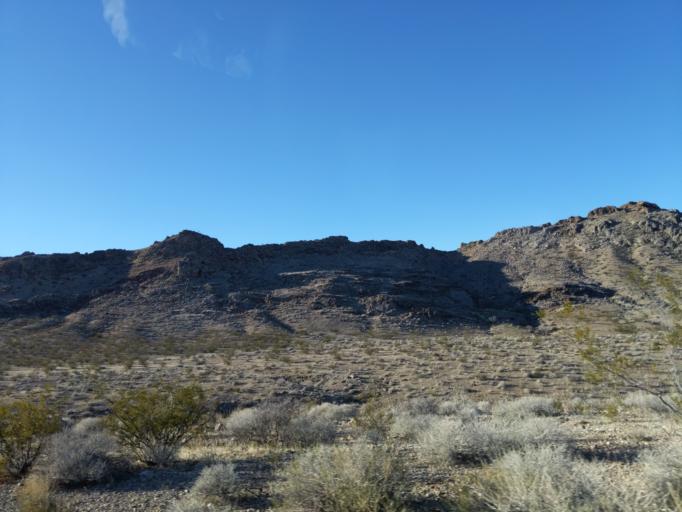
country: US
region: Nevada
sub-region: Clark County
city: Moapa Valley
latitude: 36.4168
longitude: -114.6026
